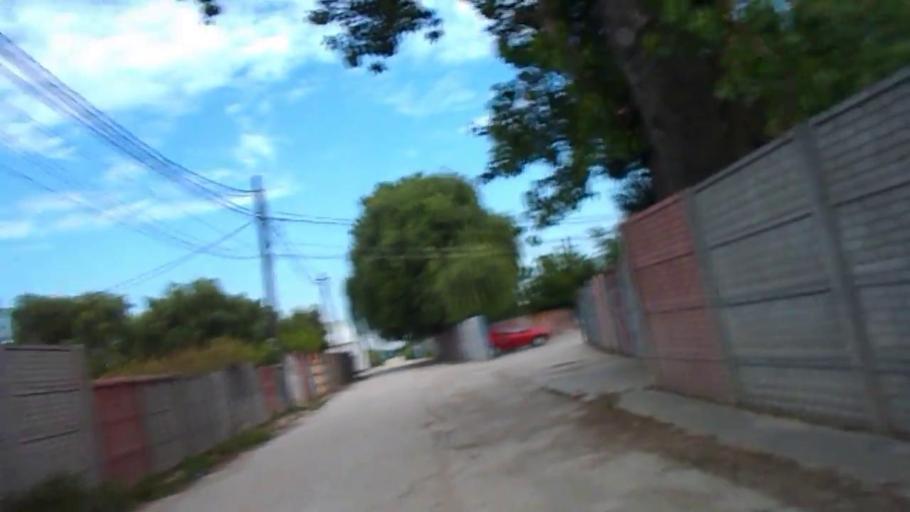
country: RO
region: Ilfov
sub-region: Comuna Jilava
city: Jilava
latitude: 44.3277
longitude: 26.0703
